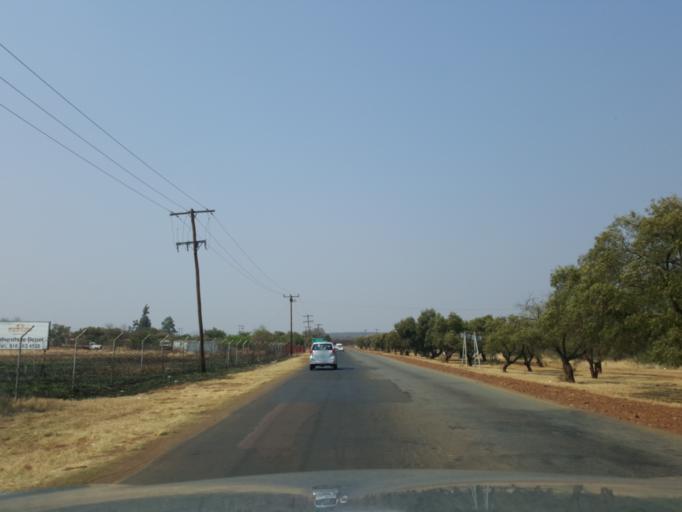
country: ZA
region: North-West
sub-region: Ngaka Modiri Molema District Municipality
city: Zeerust
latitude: -25.5007
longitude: 25.9840
